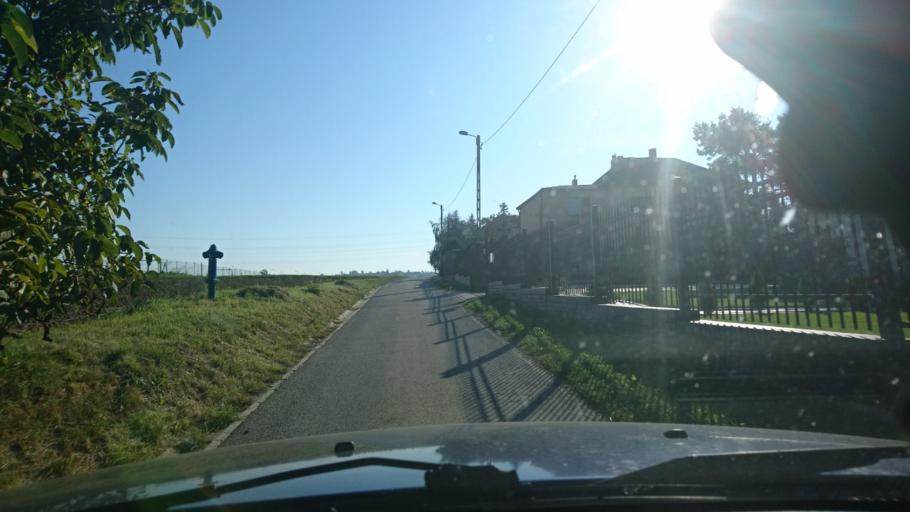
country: PL
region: Silesian Voivodeship
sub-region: Bielsko-Biala
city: Bielsko-Biala
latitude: 49.8464
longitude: 19.0575
